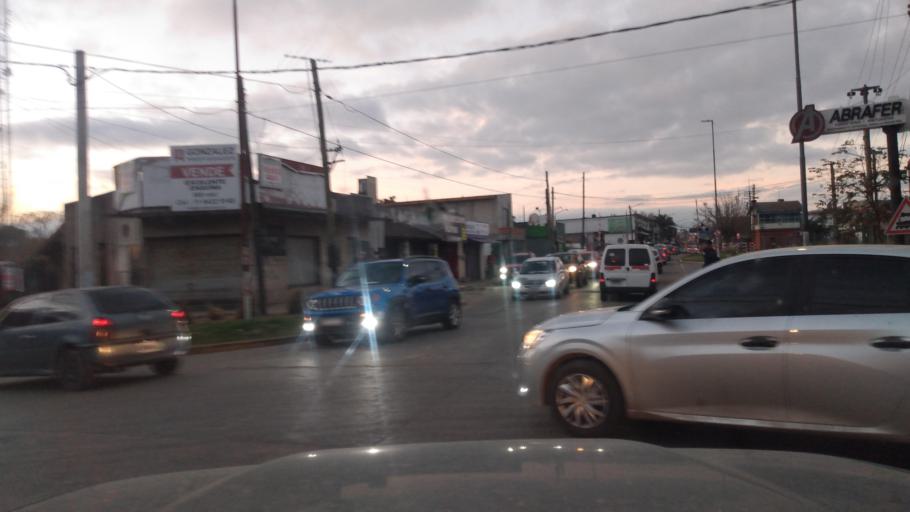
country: AR
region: Buenos Aires
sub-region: Partido de Pilar
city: Pilar
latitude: -34.4671
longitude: -58.9158
